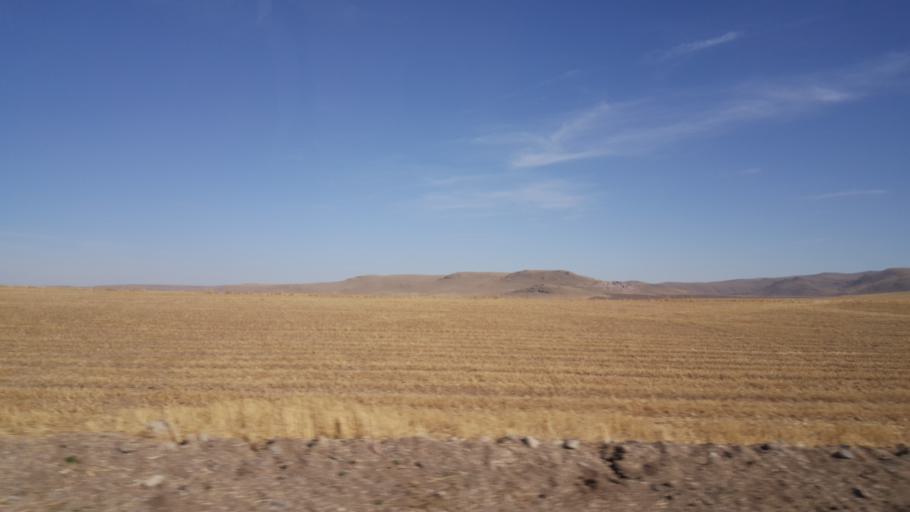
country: TR
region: Ankara
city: Yenice
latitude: 39.3268
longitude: 32.7550
